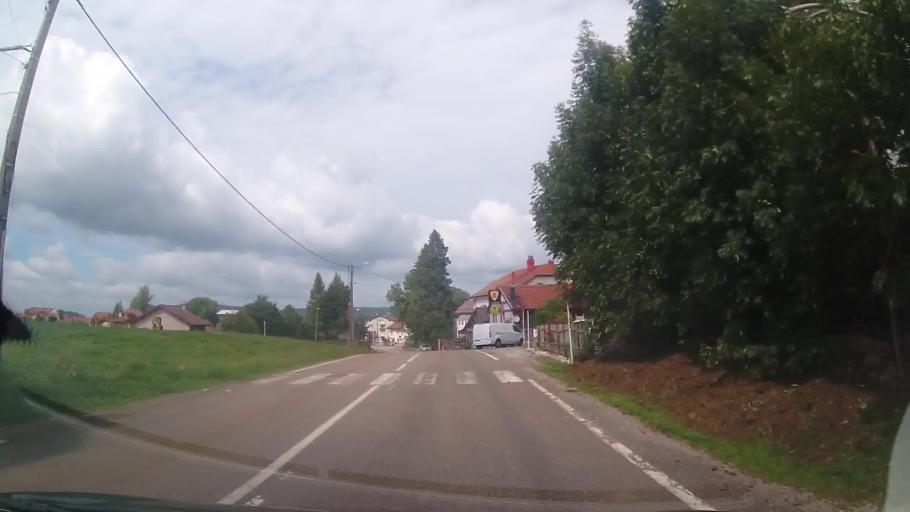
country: FR
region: Franche-Comte
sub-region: Departement du Jura
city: Les Rousses
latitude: 46.4634
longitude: 6.0725
